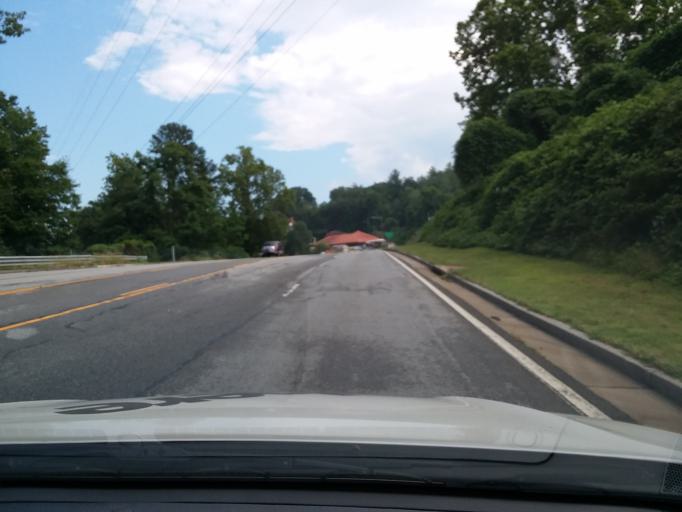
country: US
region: Georgia
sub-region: Rabun County
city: Clayton
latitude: 34.7380
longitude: -83.3937
